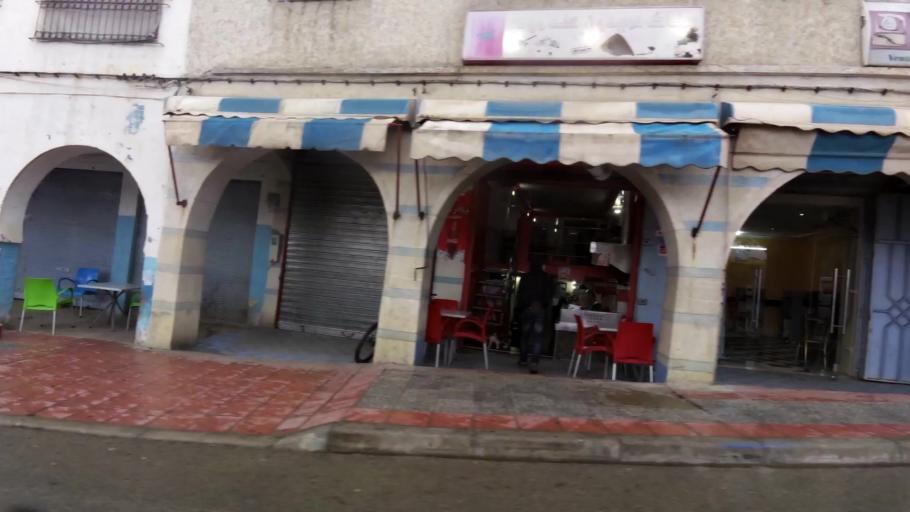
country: MA
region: Tanger-Tetouan
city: Chefchaouene
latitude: 35.1697
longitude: -5.2705
